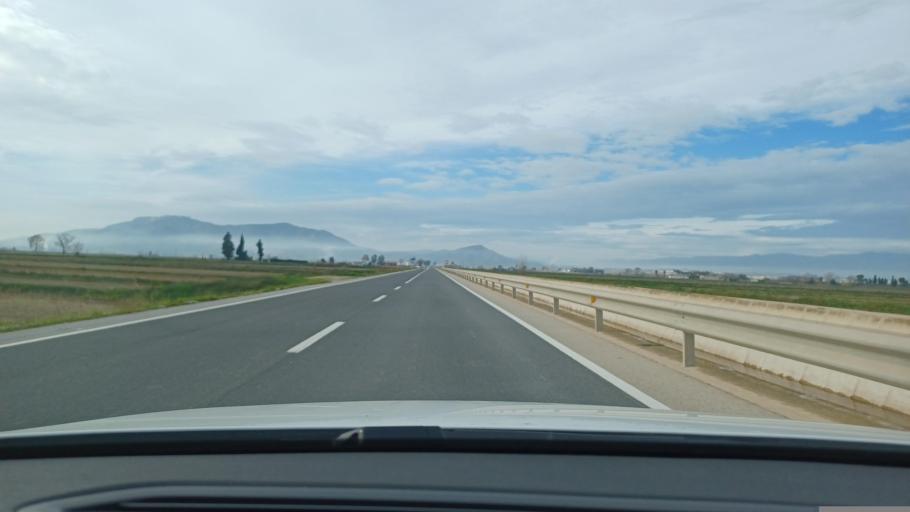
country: ES
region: Catalonia
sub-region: Provincia de Tarragona
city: Amposta
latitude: 40.7089
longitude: 0.6443
